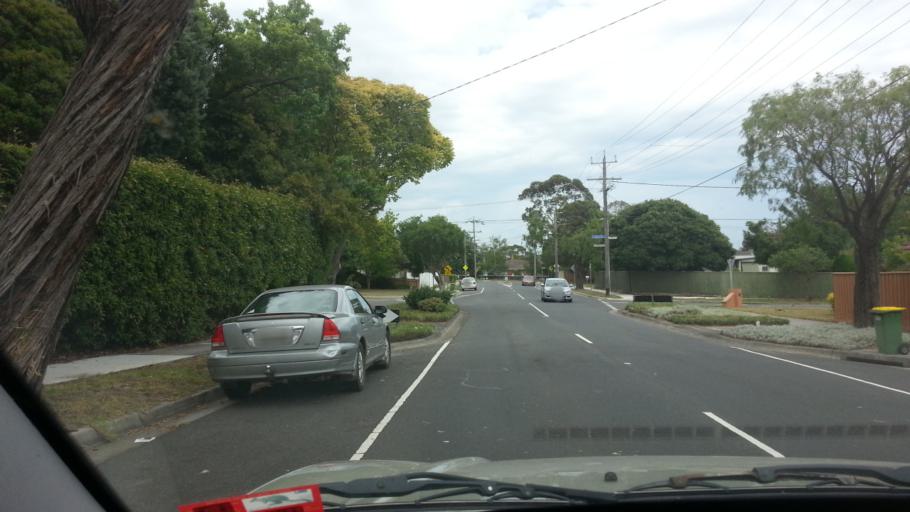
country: AU
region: Victoria
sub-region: Knox
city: Bayswater
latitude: -37.8593
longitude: 145.2521
